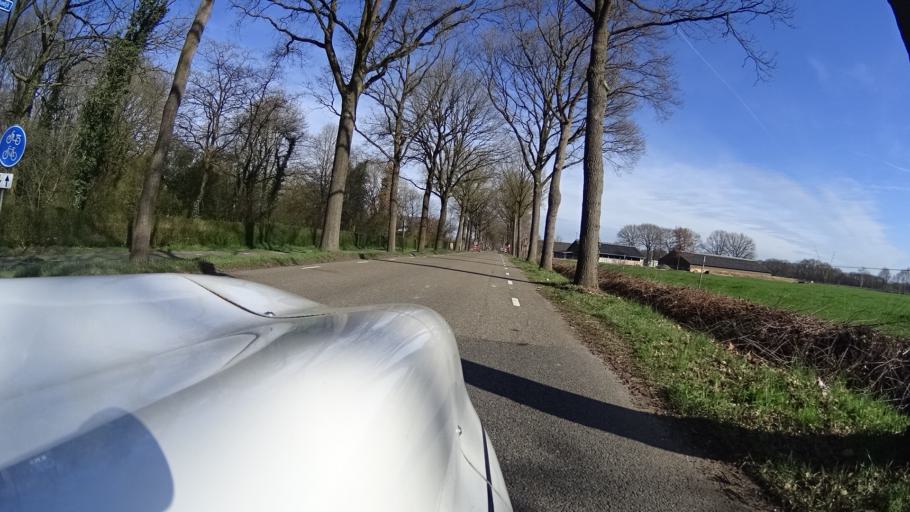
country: NL
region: North Brabant
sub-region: Gemeente Uden
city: Volkel
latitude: 51.6663
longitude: 5.6731
